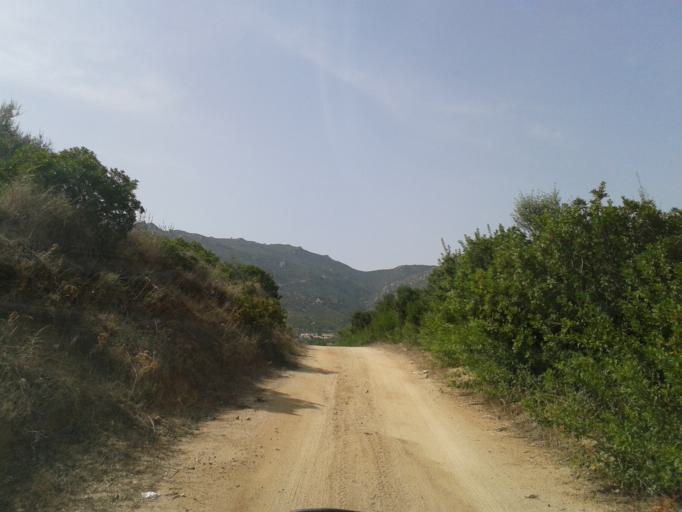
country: IT
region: Sardinia
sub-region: Provincia di Cagliari
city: Villasimius
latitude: 39.1379
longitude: 9.5002
